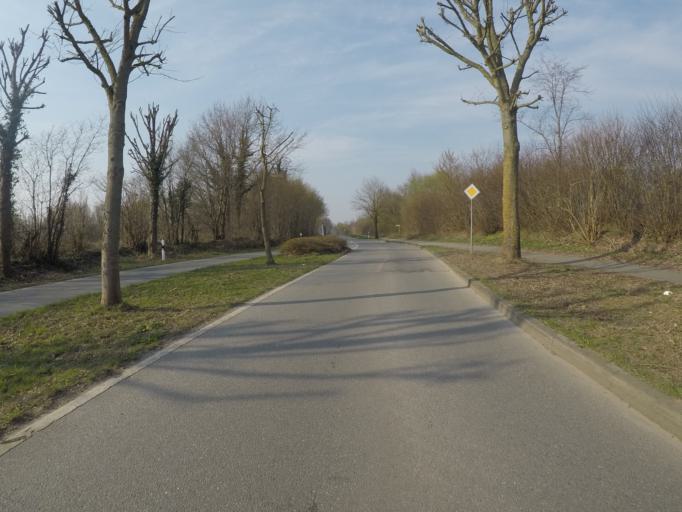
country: DE
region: Schleswig-Holstein
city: Kukels
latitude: 53.9036
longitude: 10.2316
